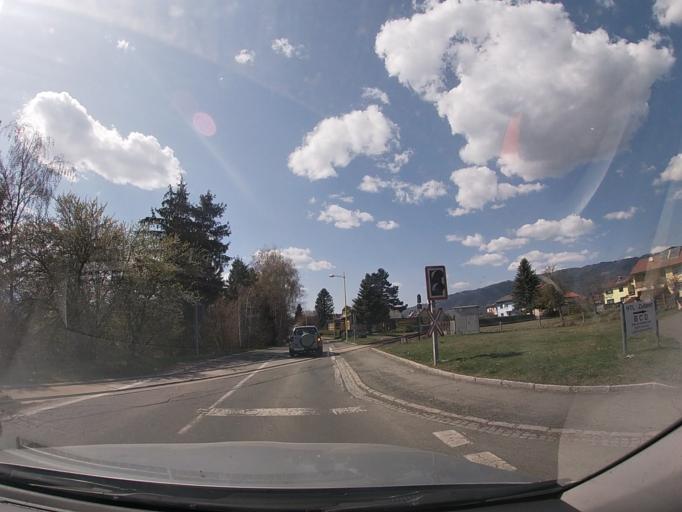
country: AT
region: Styria
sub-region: Politischer Bezirk Murtal
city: Zeltweg
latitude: 47.1908
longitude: 14.7352
